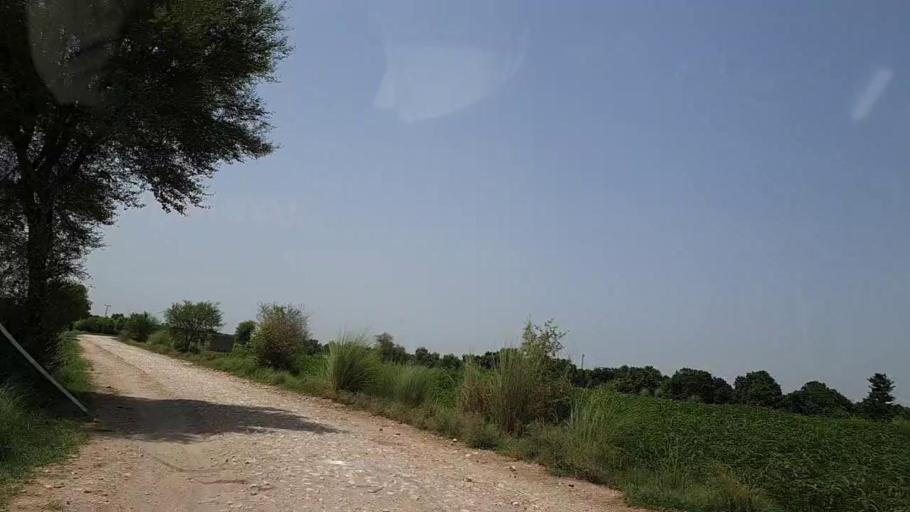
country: PK
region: Sindh
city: Tharu Shah
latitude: 26.9602
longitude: 68.0435
